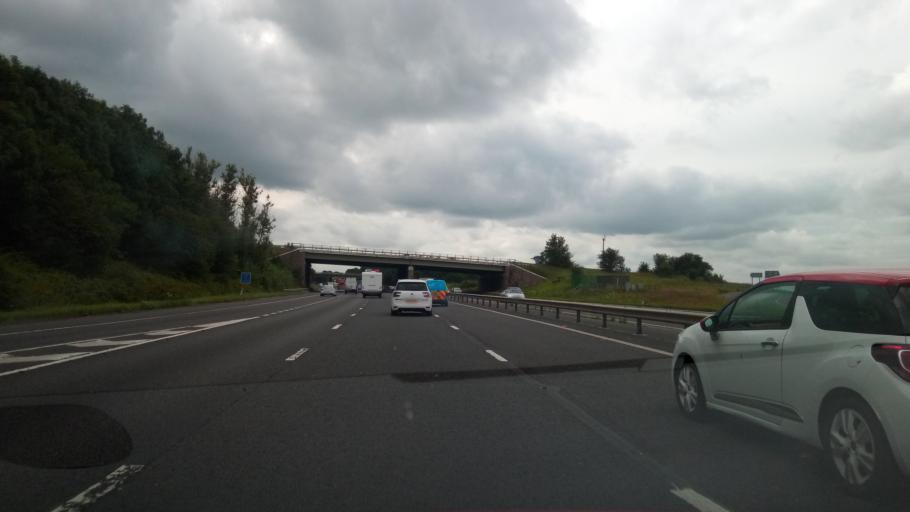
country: GB
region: England
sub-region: Lancashire
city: Galgate
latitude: 53.9841
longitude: -2.7811
